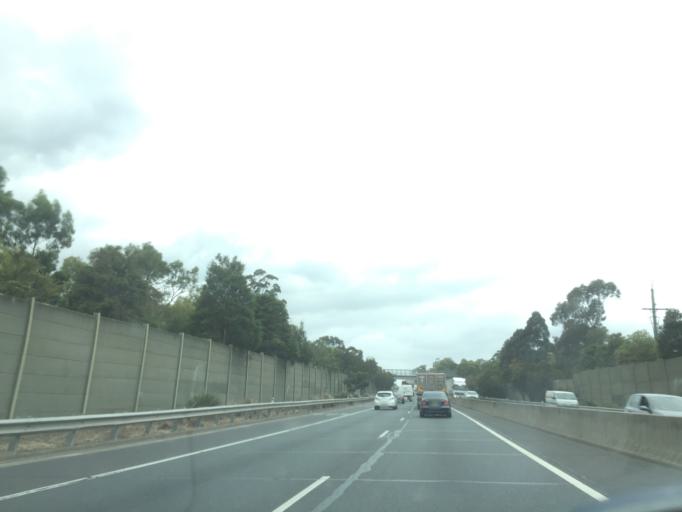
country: AU
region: New South Wales
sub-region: Parramatta
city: Northmead
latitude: -33.7725
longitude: 150.9760
